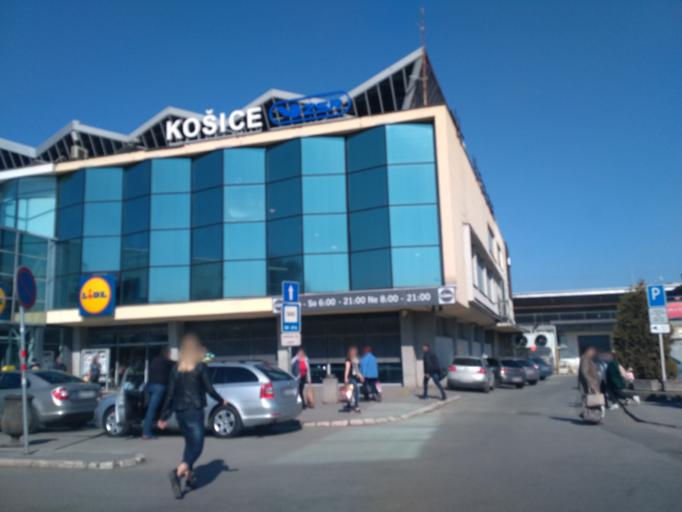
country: SK
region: Kosicky
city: Kosice
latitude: 48.7220
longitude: 21.2675
